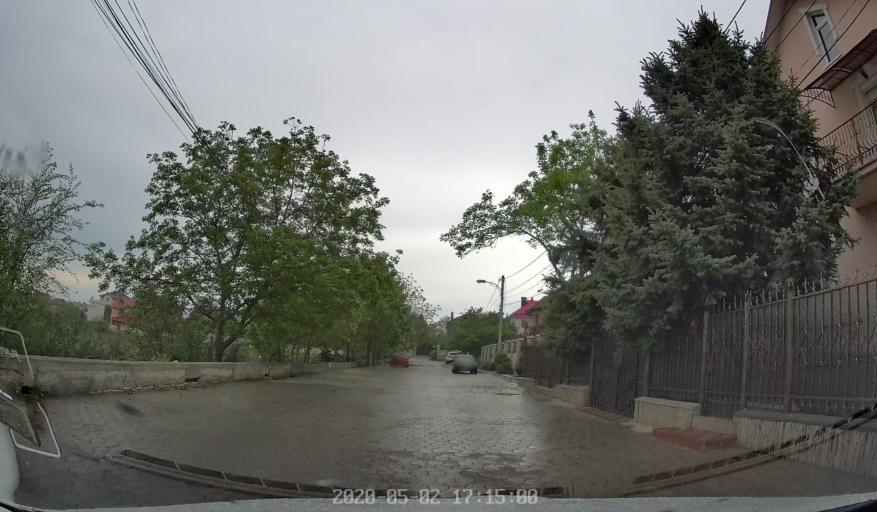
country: MD
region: Chisinau
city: Chisinau
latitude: 46.9876
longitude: 28.8251
